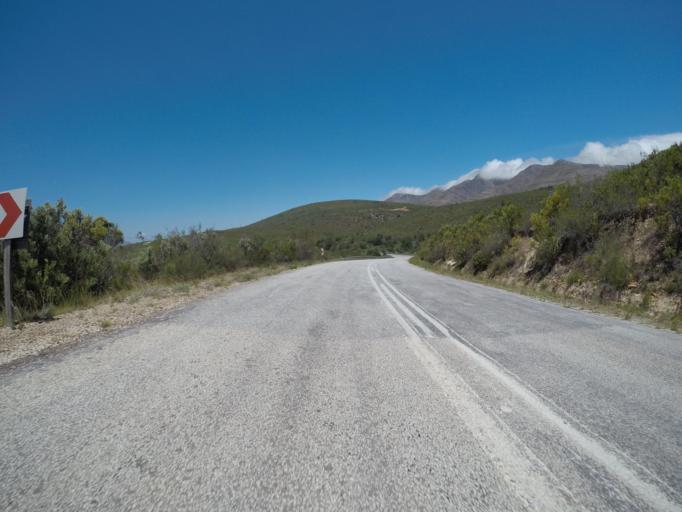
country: ZA
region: Eastern Cape
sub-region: Cacadu District Municipality
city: Kareedouw
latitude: -33.8850
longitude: 24.0763
